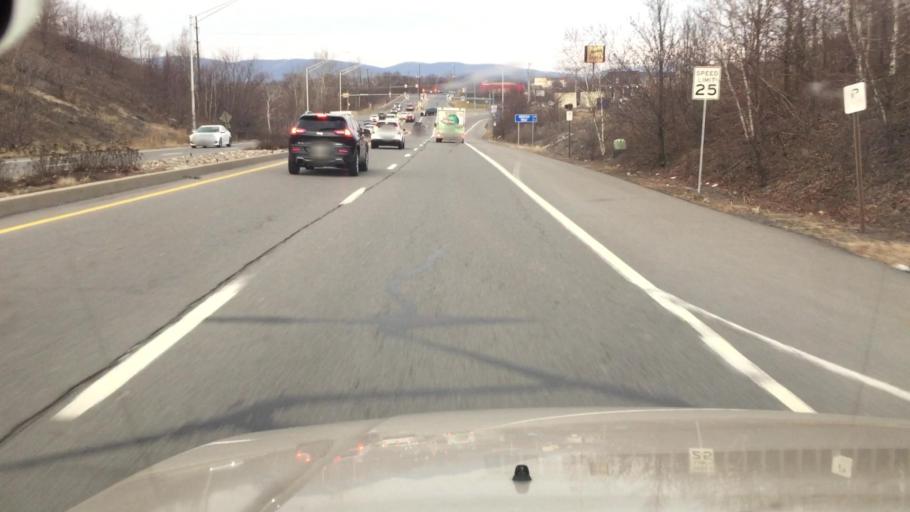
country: US
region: Pennsylvania
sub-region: Luzerne County
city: Georgetown
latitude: 41.2417
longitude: -75.8495
